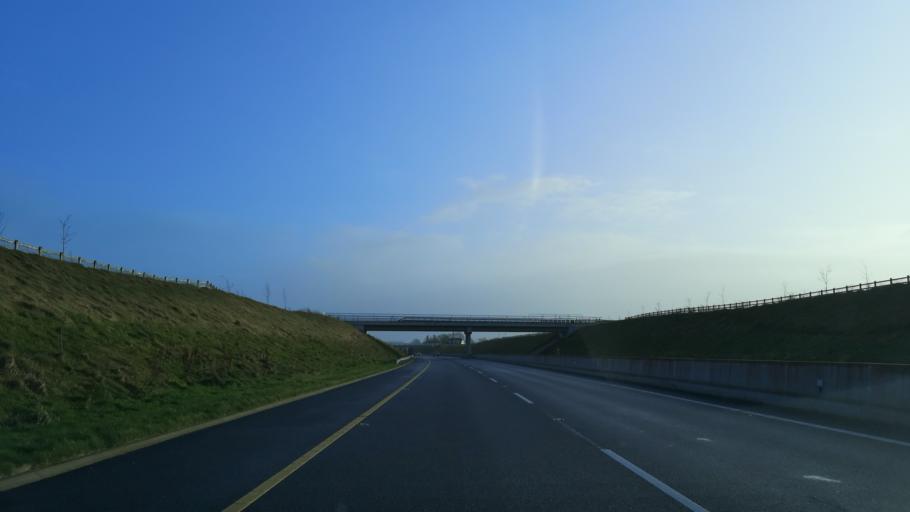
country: IE
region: Connaught
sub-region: County Galway
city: Tuam
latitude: 53.4402
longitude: -8.8478
